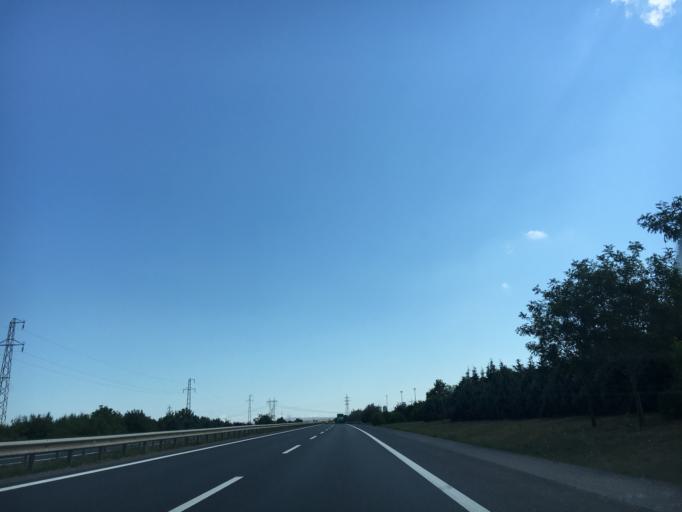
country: TR
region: Istanbul
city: Canta
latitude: 41.0866
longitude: 28.1379
